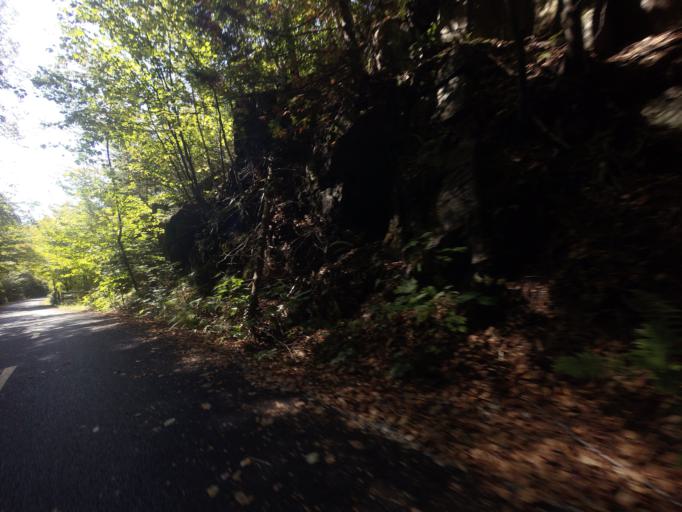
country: CA
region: Quebec
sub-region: Laurentides
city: Mont-Tremblant
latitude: 46.1341
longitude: -74.4826
